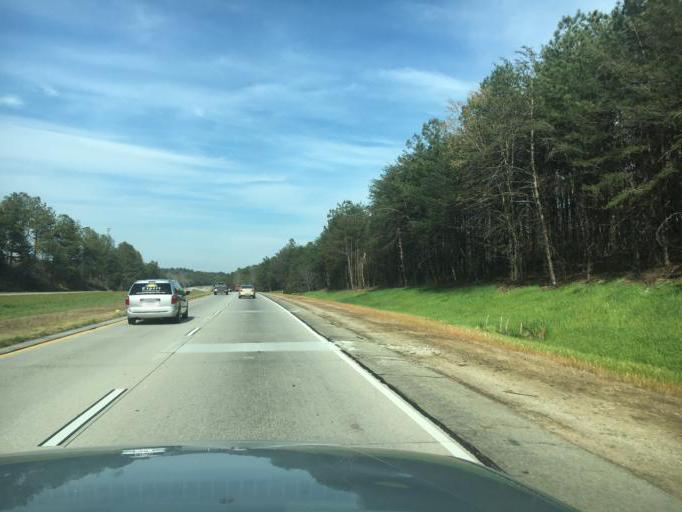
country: US
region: Georgia
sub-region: Hall County
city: Lula
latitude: 34.3679
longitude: -83.7340
